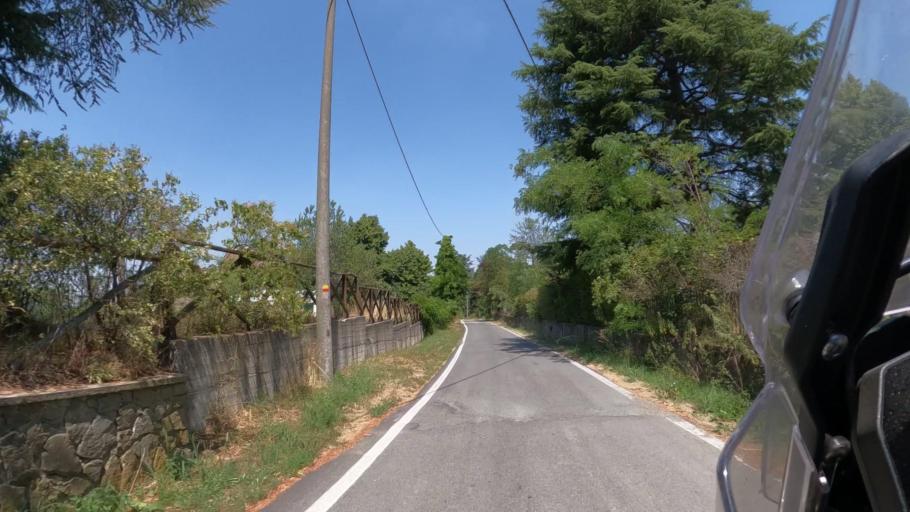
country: IT
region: Piedmont
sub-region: Provincia di Alessandria
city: Ponzone
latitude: 44.5497
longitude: 8.4826
